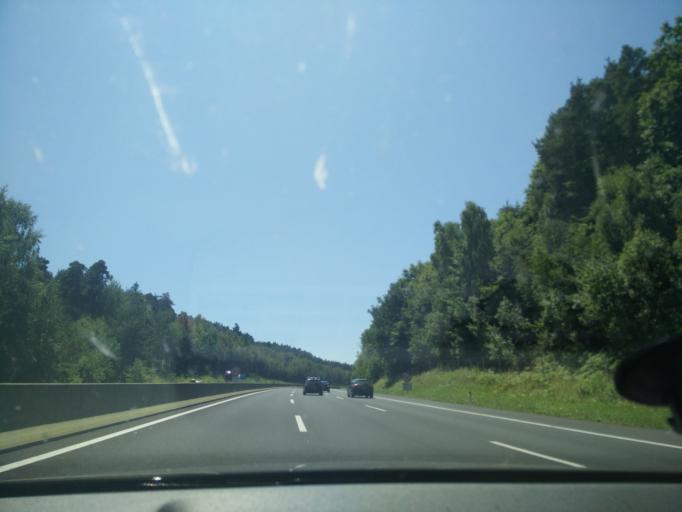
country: AT
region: Styria
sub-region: Politischer Bezirk Hartberg-Fuerstenfeld
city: Bad Waltersdorf
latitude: 47.1593
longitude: 16.0014
